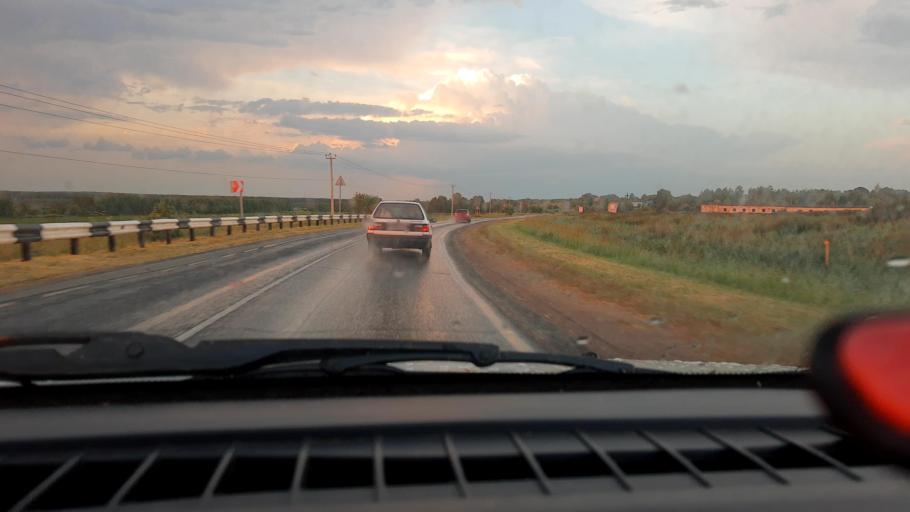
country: RU
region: Nizjnij Novgorod
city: Afonino
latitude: 56.1282
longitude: 44.0076
